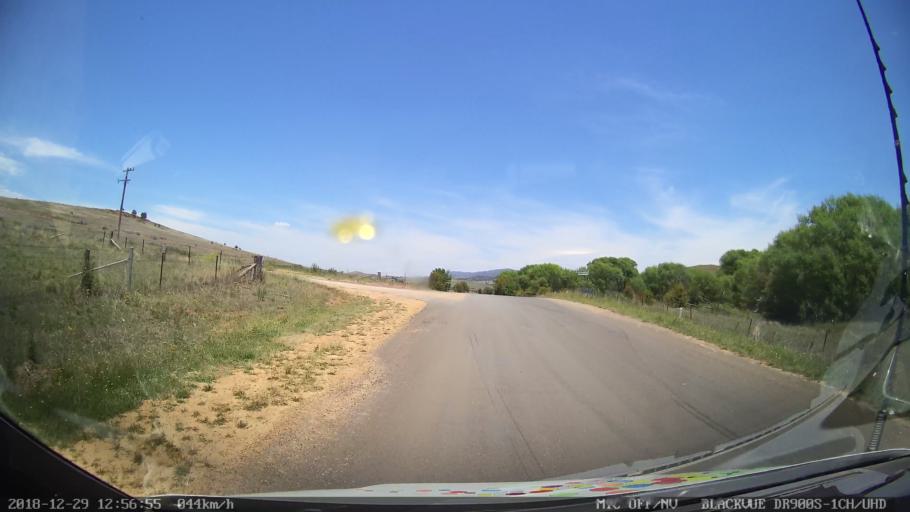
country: AU
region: Australian Capital Territory
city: Macarthur
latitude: -35.7044
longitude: 149.1802
